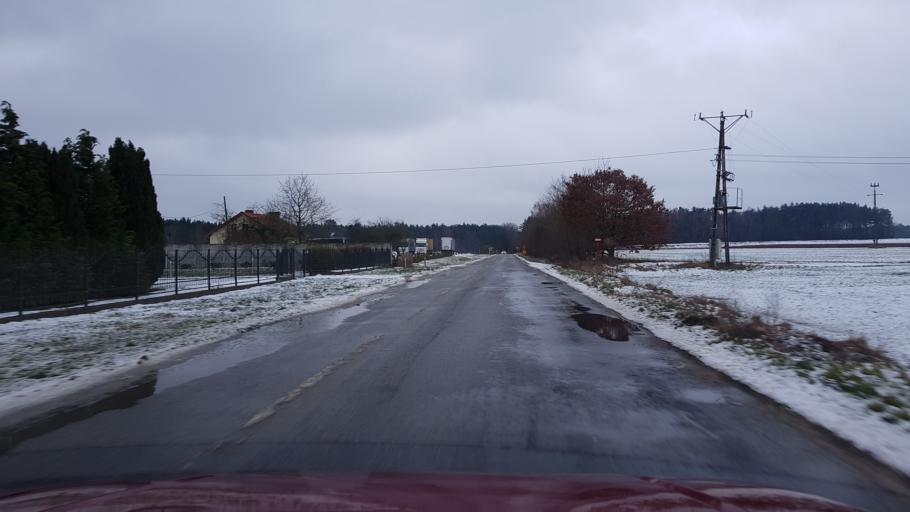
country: PL
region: West Pomeranian Voivodeship
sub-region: Powiat goleniowski
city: Nowogard
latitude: 53.6443
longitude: 15.1224
